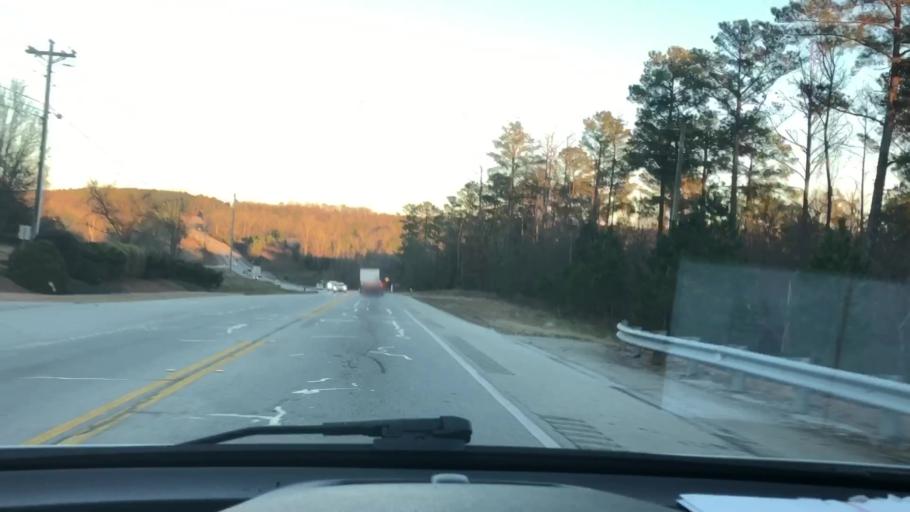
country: US
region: Georgia
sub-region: Walton County
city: Loganville
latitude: 33.8805
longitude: -83.8286
